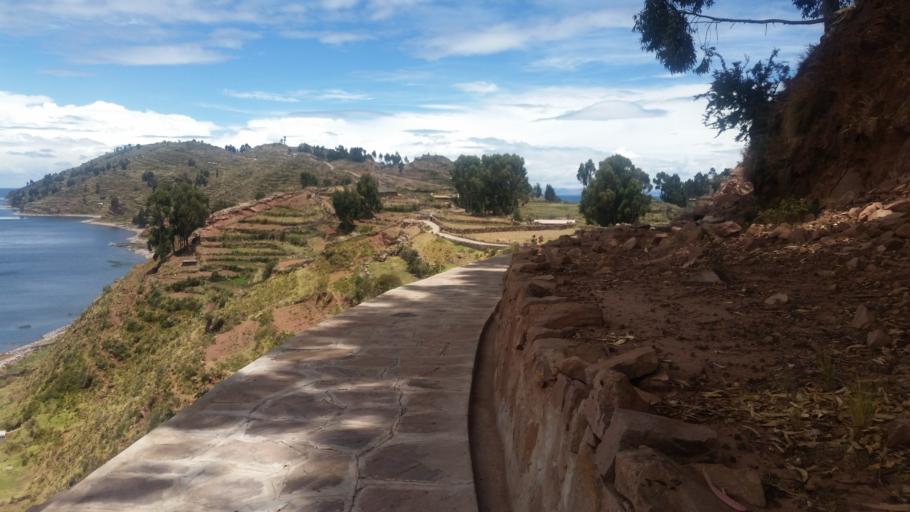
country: PE
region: Puno
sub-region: Provincia de Puno
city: Taquile
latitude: -15.7898
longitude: -69.6824
